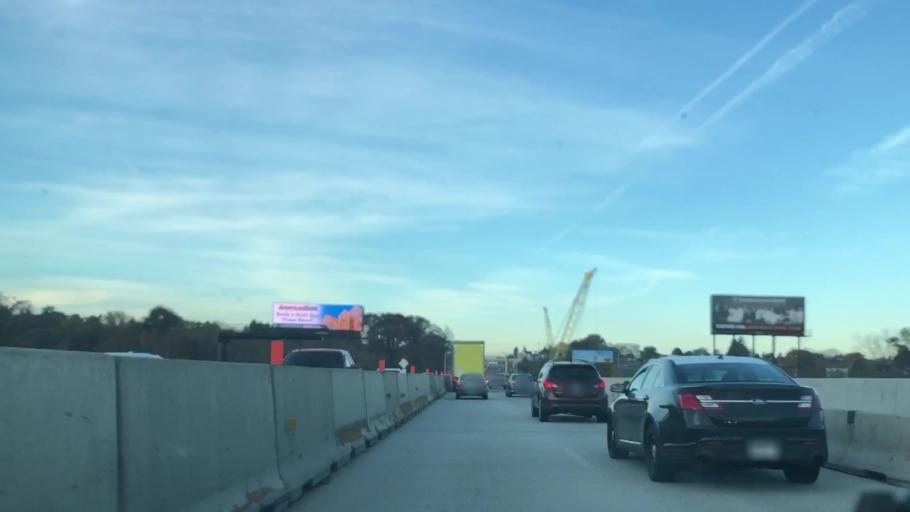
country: US
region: Pennsylvania
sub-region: Lehigh County
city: Fullerton
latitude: 40.6330
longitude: -75.4625
